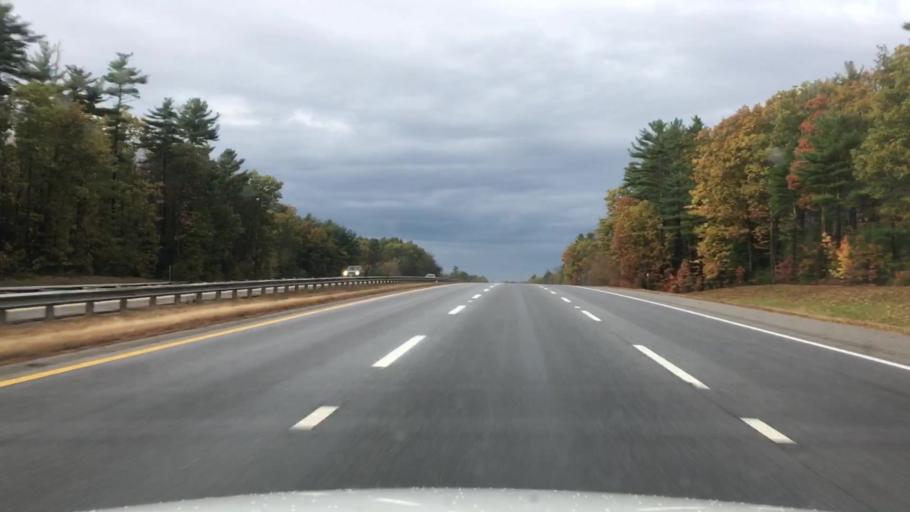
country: US
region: Maine
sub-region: York County
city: Biddeford
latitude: 43.4718
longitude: -70.5101
